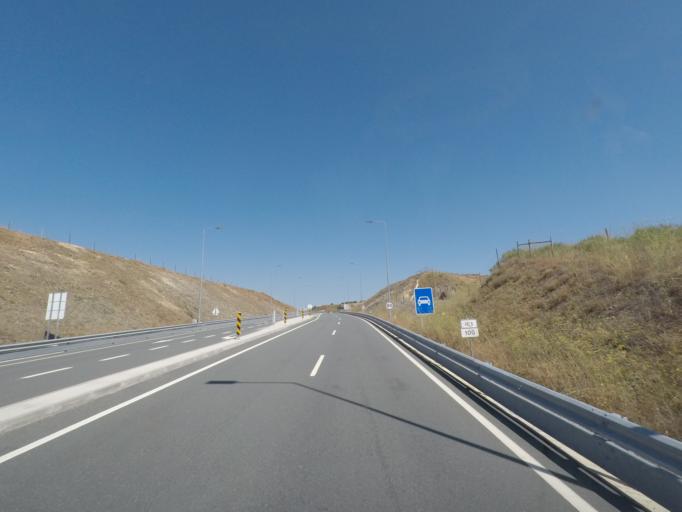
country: PT
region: Braganca
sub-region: Alfandega da Fe
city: Alfandega da Fe
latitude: 41.2813
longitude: -6.8938
